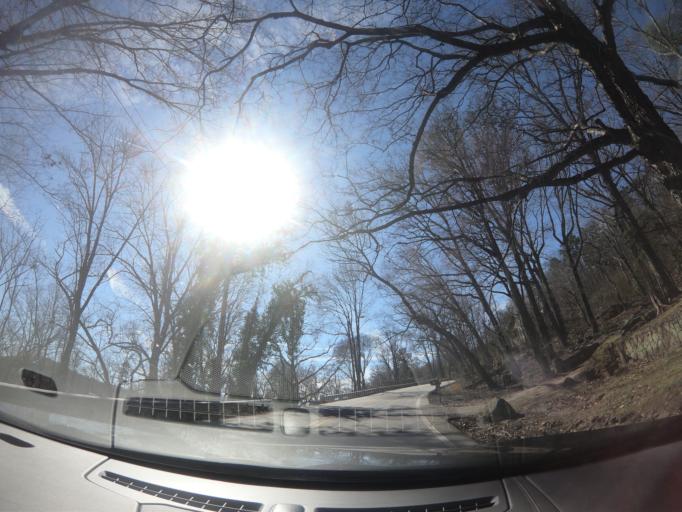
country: US
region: Tennessee
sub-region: Hamilton County
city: Lookout Mountain
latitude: 35.0054
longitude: -85.3311
